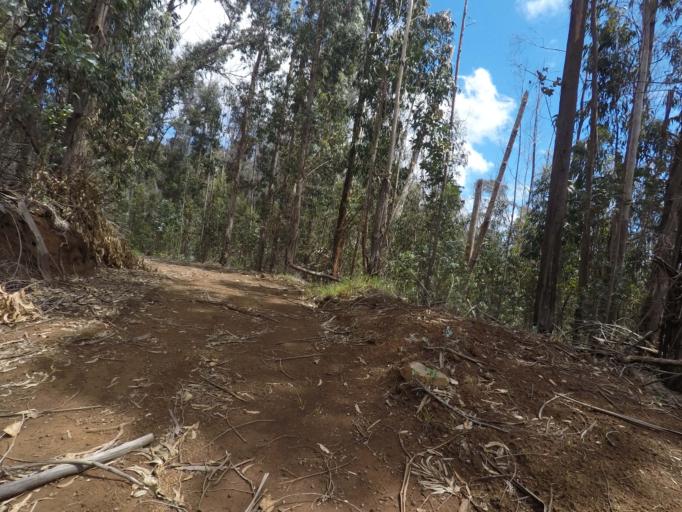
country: PT
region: Madeira
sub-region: Calheta
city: Estreito da Calheta
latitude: 32.7480
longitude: -17.1956
